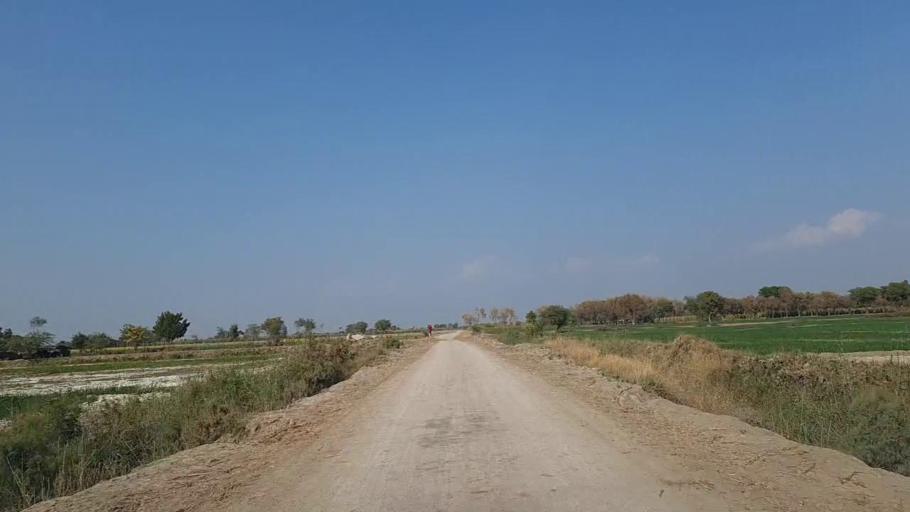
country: PK
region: Sindh
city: Jam Sahib
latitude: 26.2974
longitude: 68.5832
